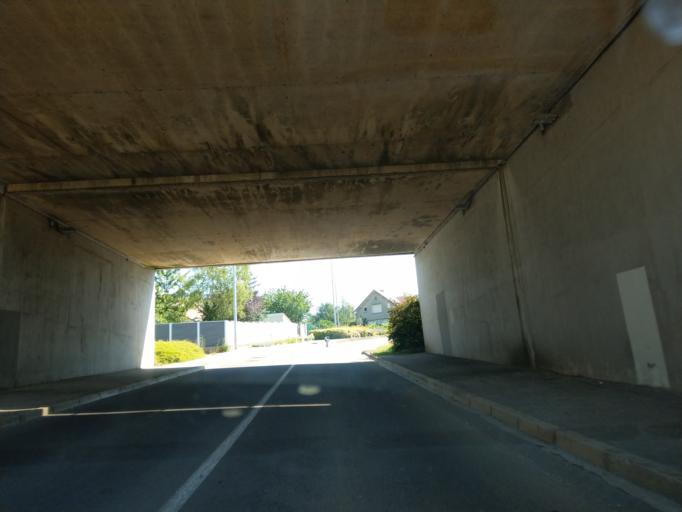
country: FR
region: Bourgogne
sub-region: Departement de la Cote-d'Or
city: Talant
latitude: 47.3379
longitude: 4.9994
